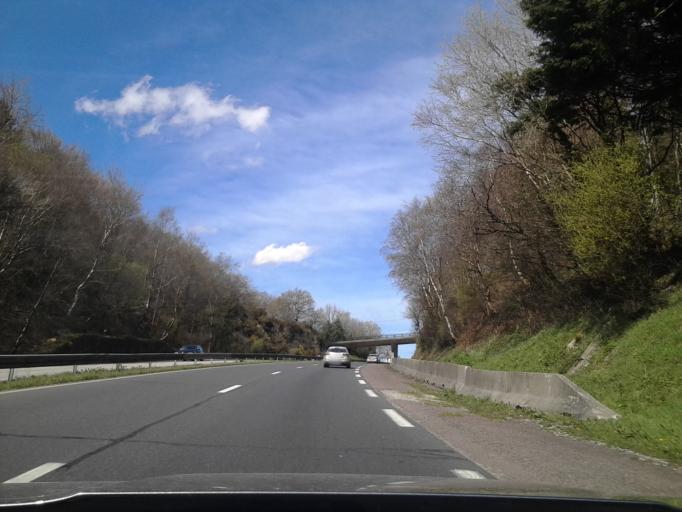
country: FR
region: Lower Normandy
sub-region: Departement de la Manche
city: Brix
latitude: 49.5478
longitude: -1.5597
